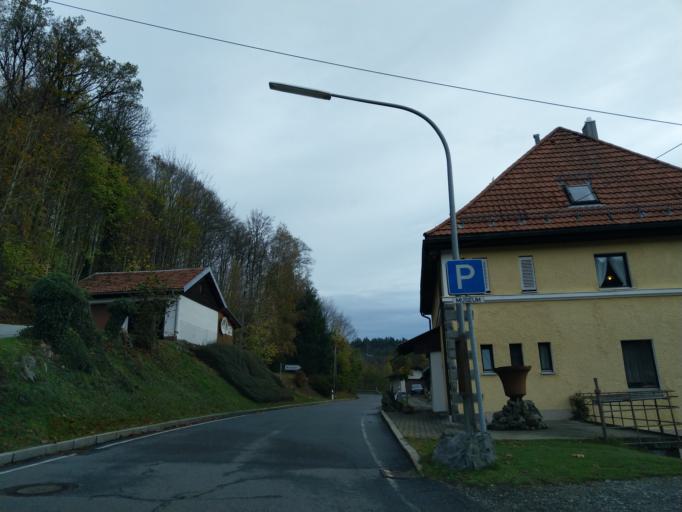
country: DE
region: Bavaria
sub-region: Lower Bavaria
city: Schofweg
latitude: 48.8150
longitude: 13.2321
